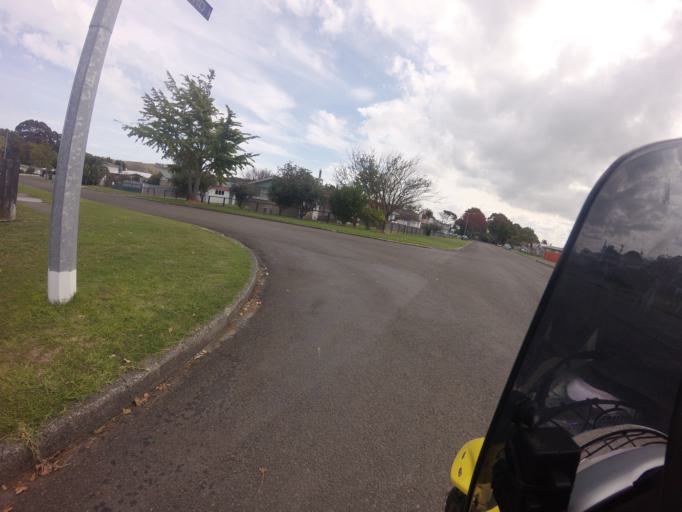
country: NZ
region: Gisborne
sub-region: Gisborne District
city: Gisborne
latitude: -38.6749
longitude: 178.0544
